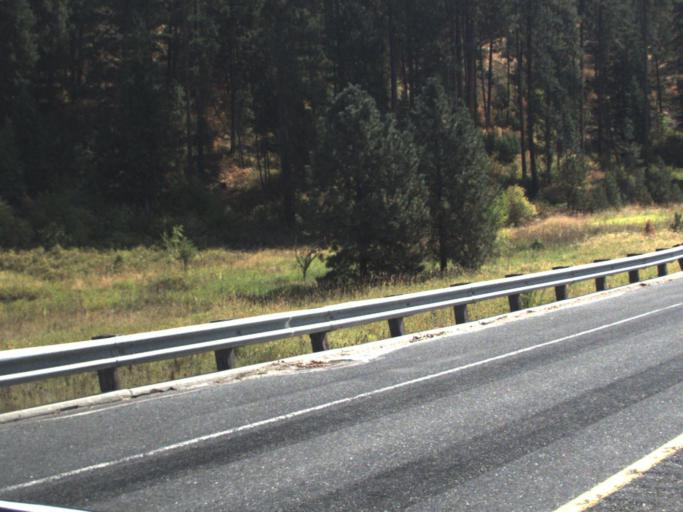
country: US
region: Washington
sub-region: Stevens County
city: Chewelah
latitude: 48.3626
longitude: -117.8361
